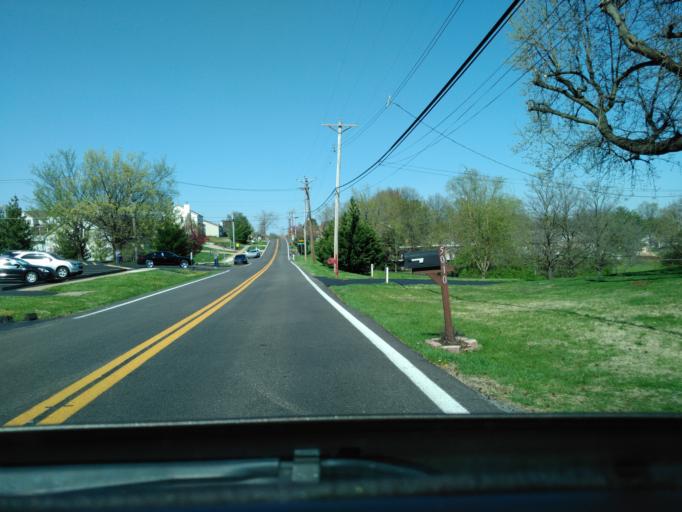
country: US
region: Missouri
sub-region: Saint Louis County
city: Concord
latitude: 38.4934
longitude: -90.3678
